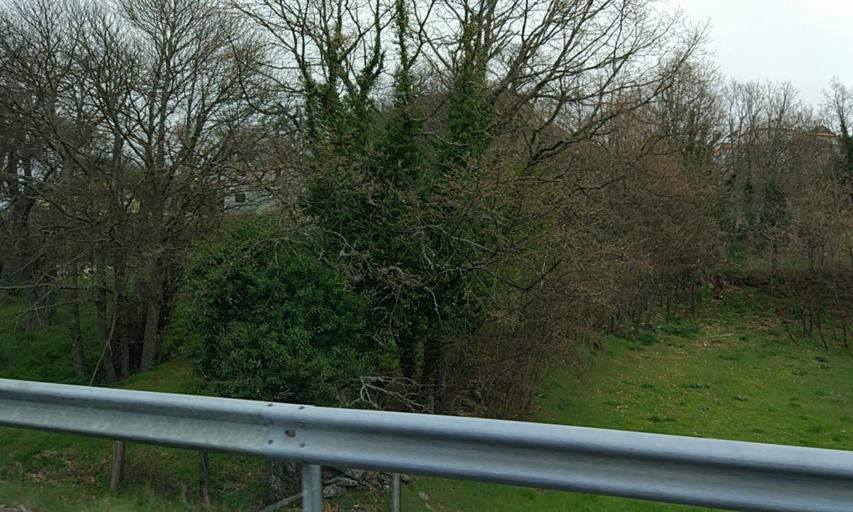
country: PT
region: Guarda
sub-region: Guarda
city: Sequeira
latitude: 40.5869
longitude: -7.2626
